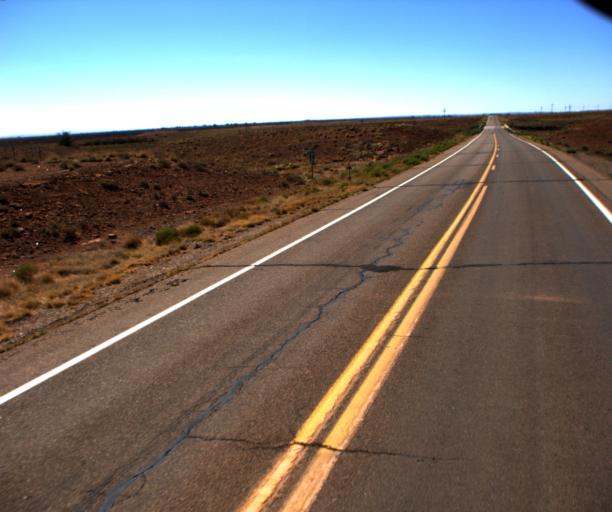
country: US
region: Arizona
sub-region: Coconino County
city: LeChee
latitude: 35.2969
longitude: -110.9933
